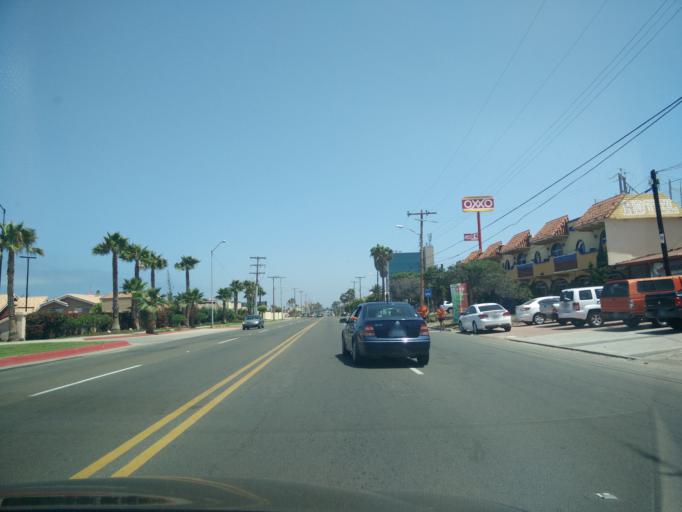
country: MX
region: Baja California
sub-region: Tijuana
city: La Esperanza [Granjas Familiares]
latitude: 32.5154
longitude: -117.1200
